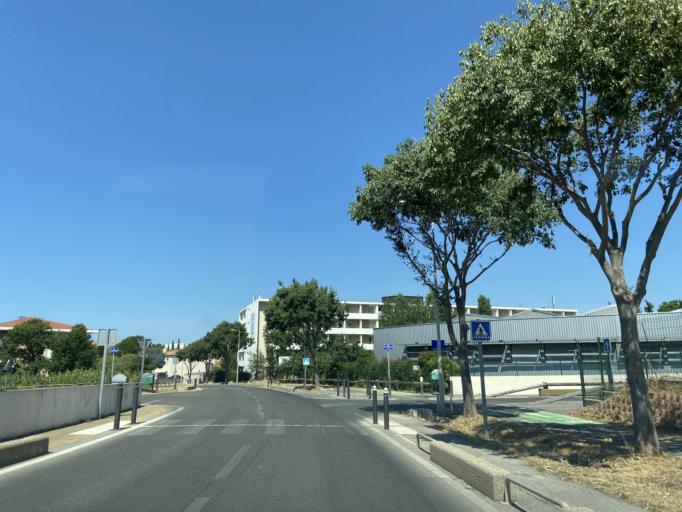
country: FR
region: Provence-Alpes-Cote d'Azur
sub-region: Departement des Bouches-du-Rhone
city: Plan-de-Cuques
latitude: 43.3442
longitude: 5.4438
